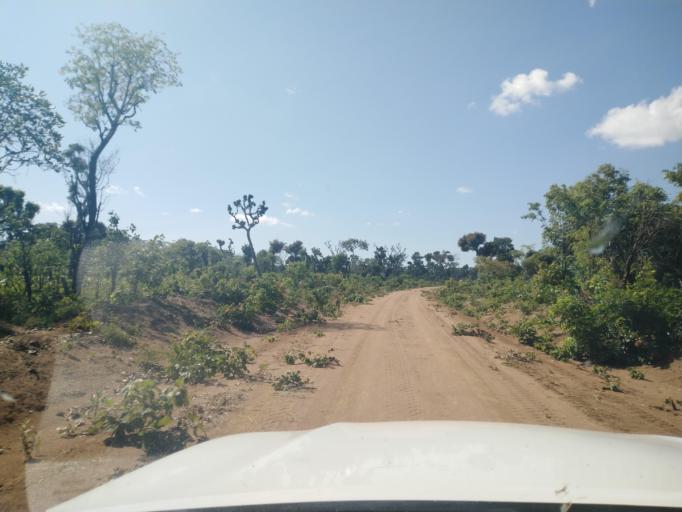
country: ZM
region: Northern
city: Chinsali
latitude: -11.0076
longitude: 31.7742
